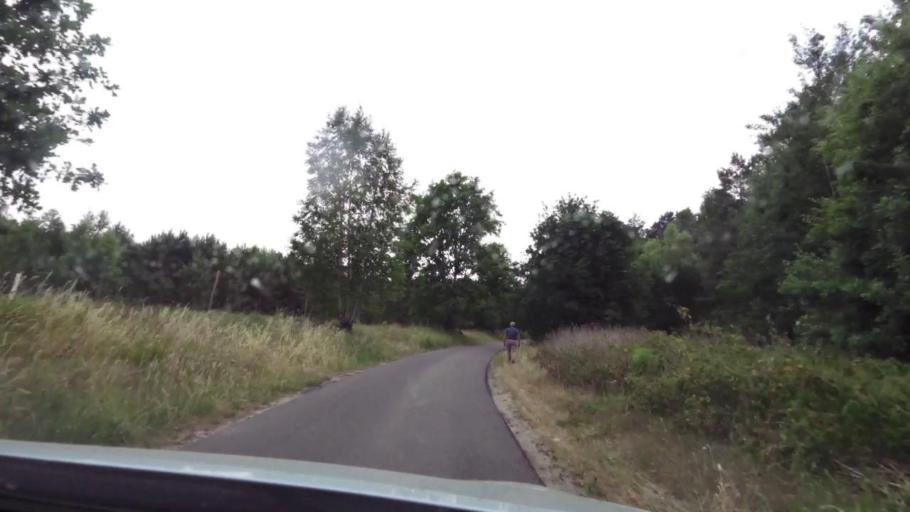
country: PL
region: Pomeranian Voivodeship
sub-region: Powiat bytowski
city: Trzebielino
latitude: 54.2568
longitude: 17.0080
